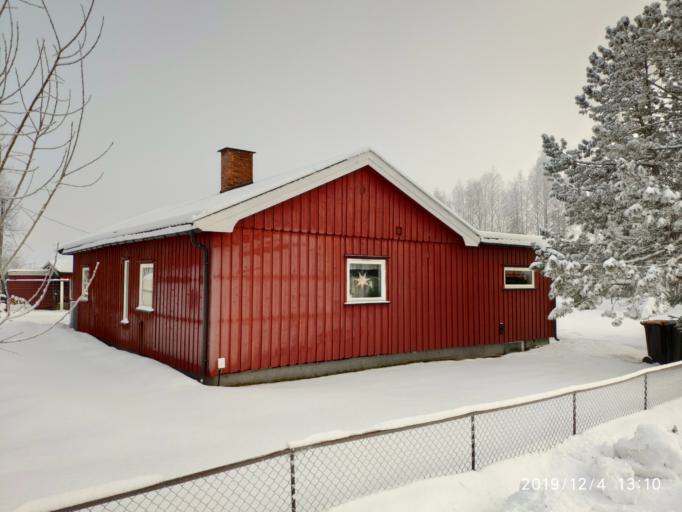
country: NO
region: Hedmark
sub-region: Elverum
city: Elverum
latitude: 60.8872
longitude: 11.5409
